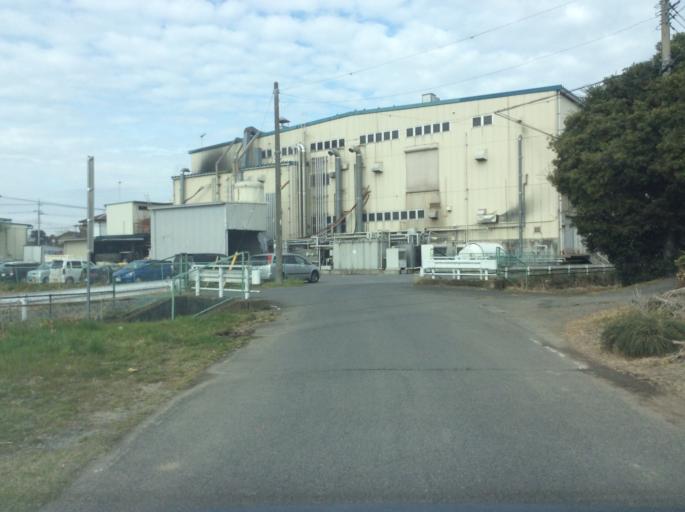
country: JP
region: Ibaraki
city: Ishige
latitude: 36.1743
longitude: 139.9595
